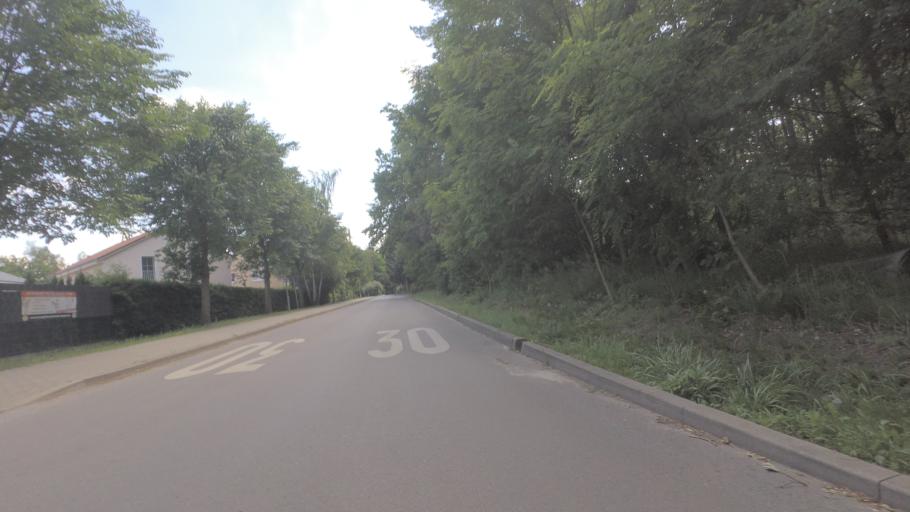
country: DE
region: Brandenburg
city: Rangsdorf
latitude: 52.2832
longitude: 13.4182
